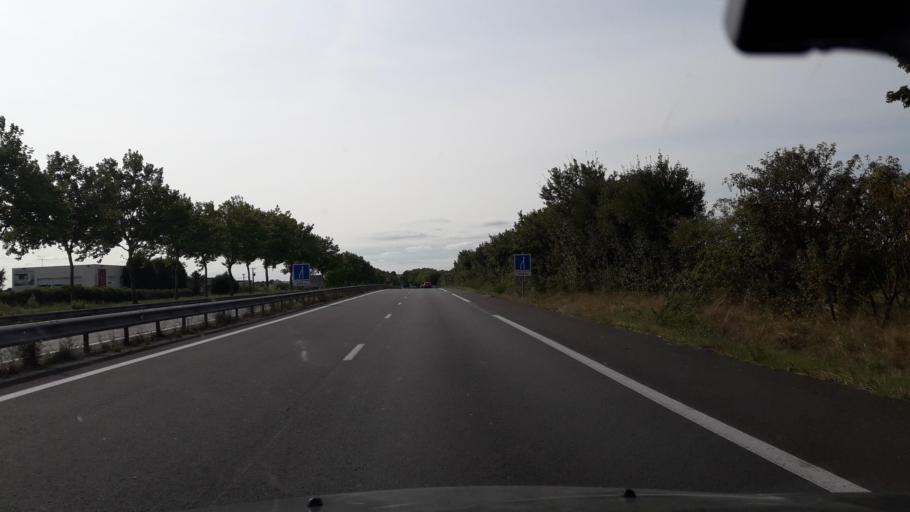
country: FR
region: Poitou-Charentes
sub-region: Departement de la Charente
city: Saint-Brice
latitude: 45.6797
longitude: -0.2854
